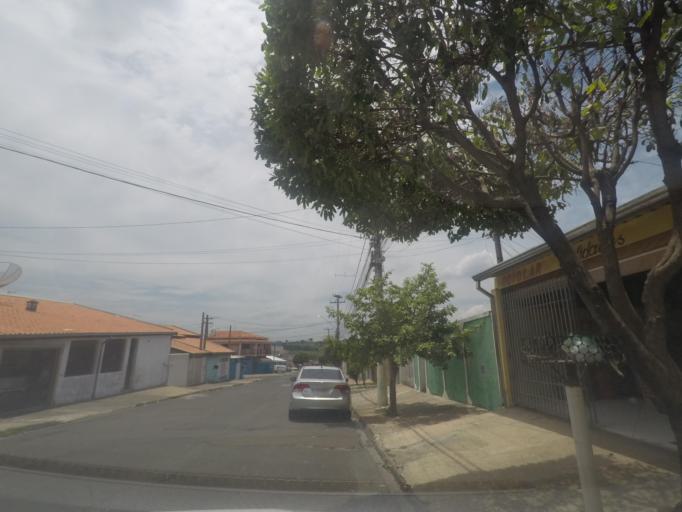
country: BR
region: Sao Paulo
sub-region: Nova Odessa
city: Nova Odessa
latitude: -22.7944
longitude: -47.2784
